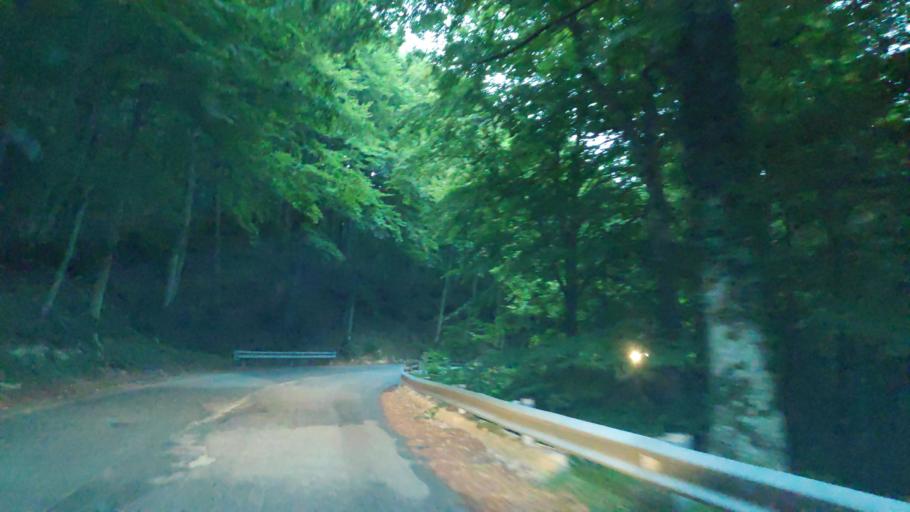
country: IT
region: Calabria
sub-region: Provincia di Vibo-Valentia
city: Mongiana
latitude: 38.5201
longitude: 16.3403
